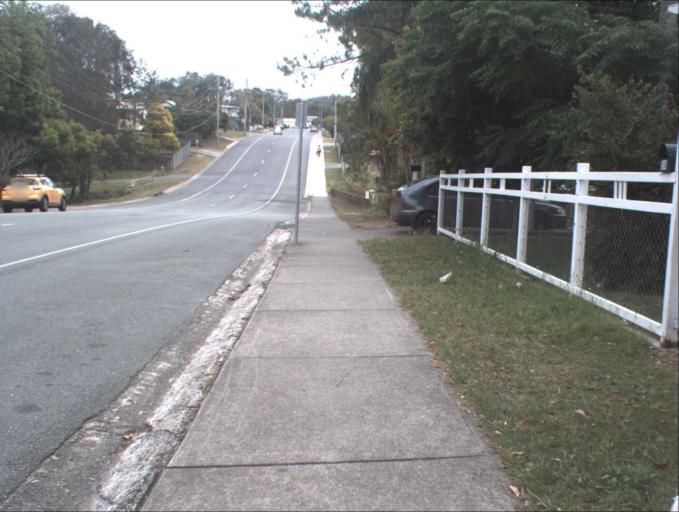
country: AU
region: Queensland
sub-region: Logan
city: Beenleigh
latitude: -27.7124
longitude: 153.1977
